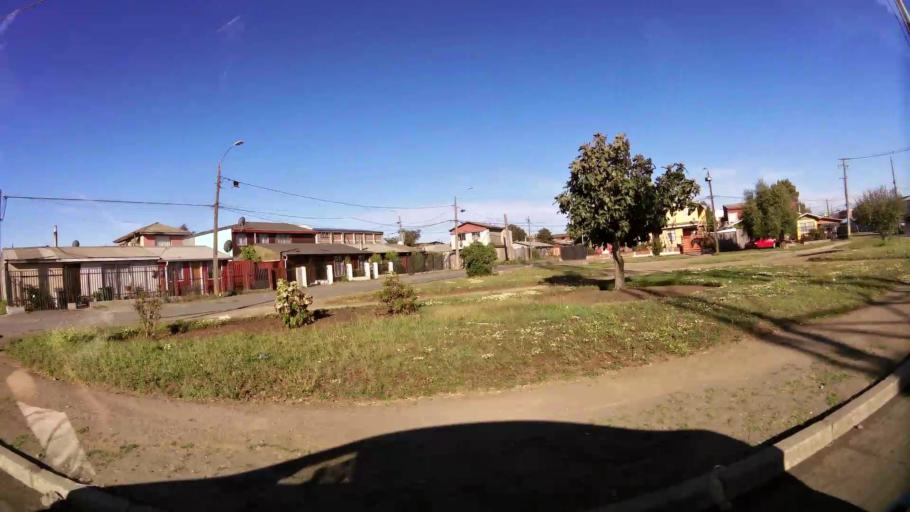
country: CL
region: Biobio
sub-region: Provincia de Concepcion
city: Concepcion
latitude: -36.8264
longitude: -73.1298
